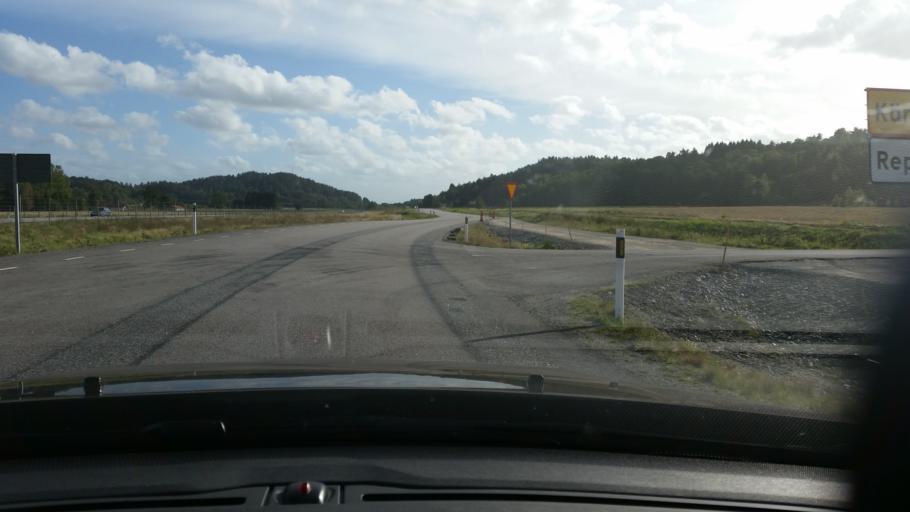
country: SE
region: Vaestra Goetaland
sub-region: Lilla Edets Kommun
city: Lodose
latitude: 58.0819
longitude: 12.1560
